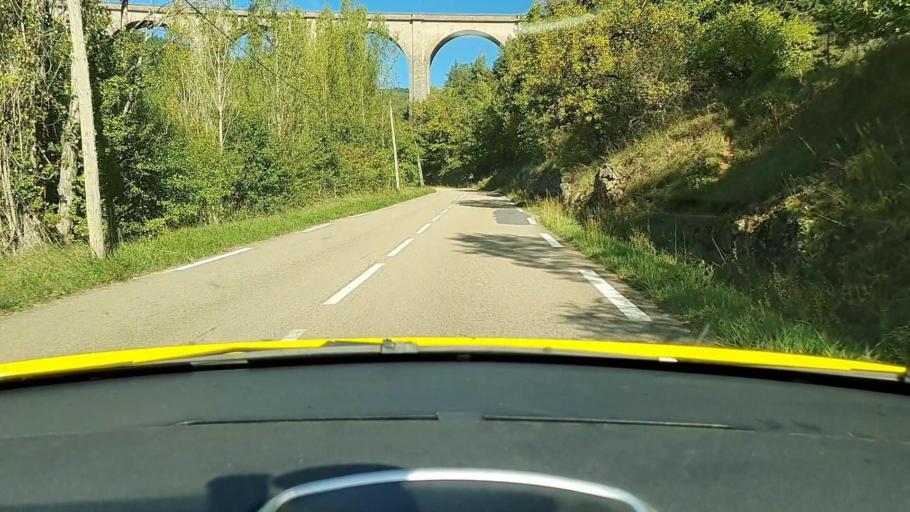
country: FR
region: Languedoc-Roussillon
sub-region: Departement du Gard
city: Le Vigan
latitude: 43.9660
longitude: 3.4306
